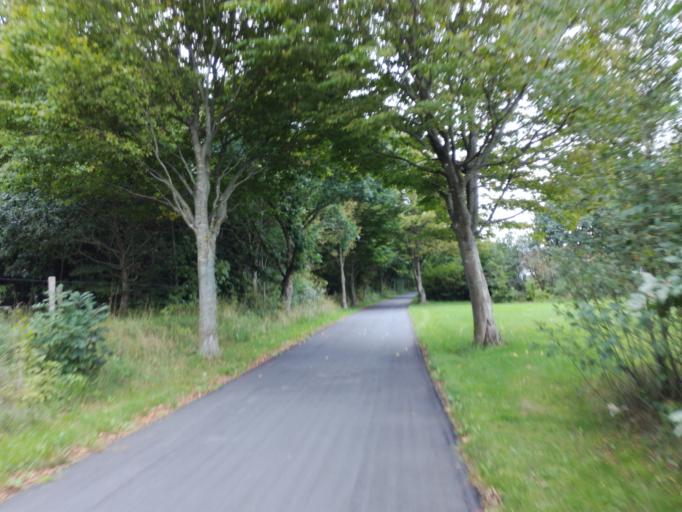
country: DK
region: South Denmark
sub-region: Vejle Kommune
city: Vejle
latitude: 55.6834
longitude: 9.5768
